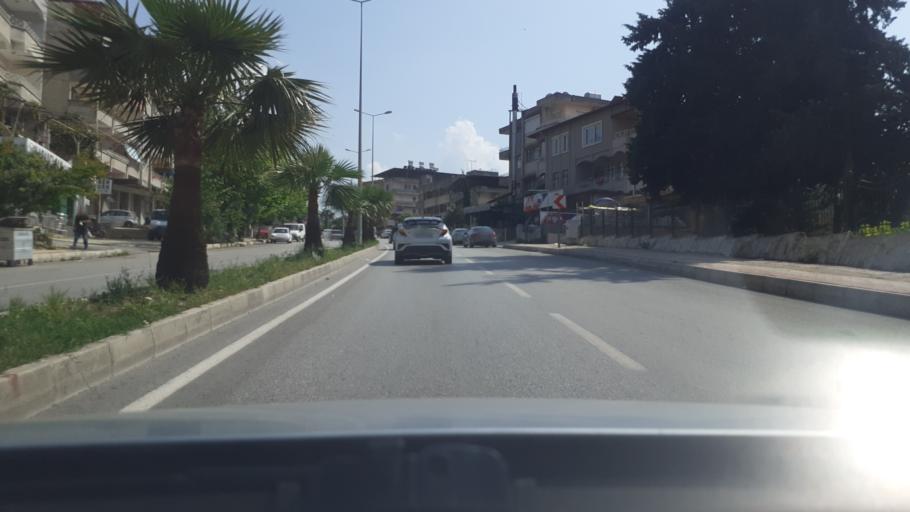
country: TR
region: Hatay
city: Gumusgoze
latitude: 36.1442
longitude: 36.1413
